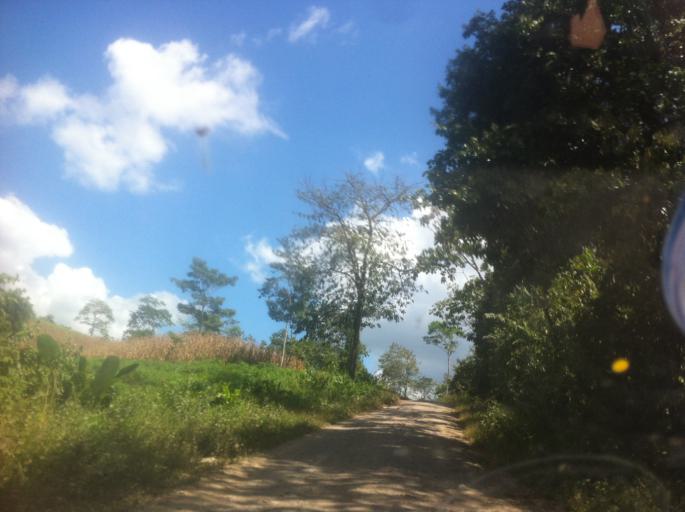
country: CR
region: Alajuela
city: Los Chiles
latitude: 11.2341
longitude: -84.4894
